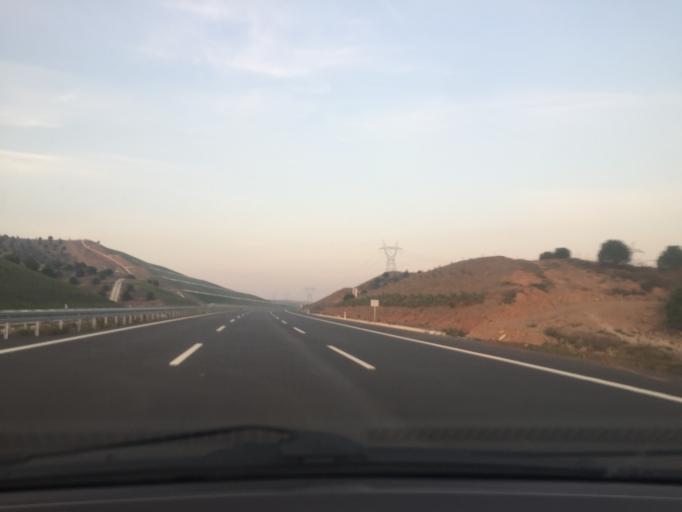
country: TR
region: Bursa
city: Mahmudiye
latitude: 40.2741
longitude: 28.5598
